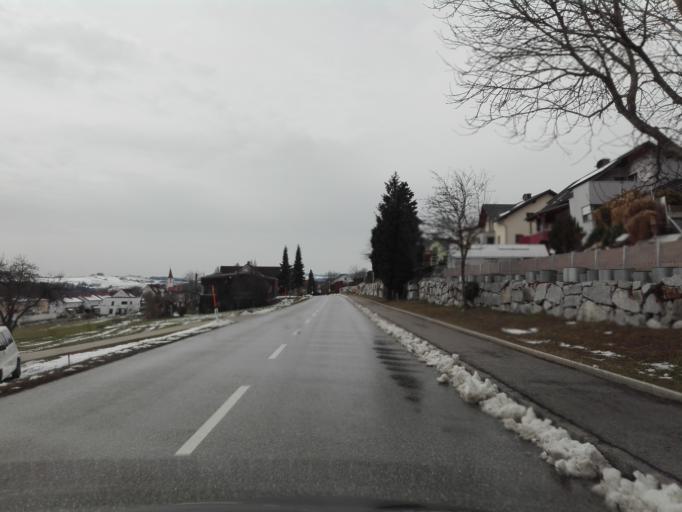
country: AT
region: Upper Austria
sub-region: Politischer Bezirk Rohrbach
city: Kleinzell im Muehlkreis
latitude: 48.4561
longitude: 14.0001
